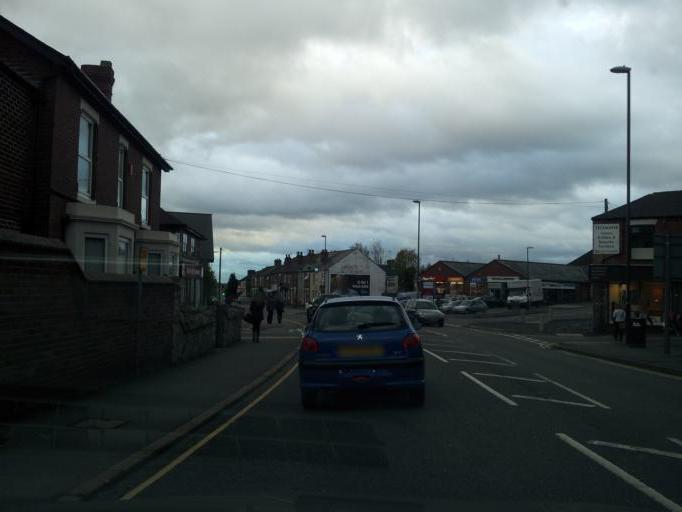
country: GB
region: England
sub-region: Derbyshire
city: Ilkeston
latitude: 52.9669
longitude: -1.3059
